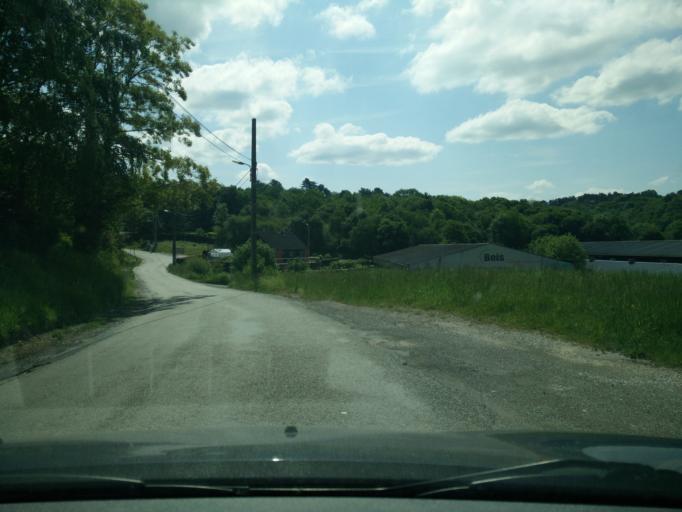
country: BE
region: Wallonia
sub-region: Province de Namur
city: Couvin
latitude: 50.0693
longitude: 4.5104
